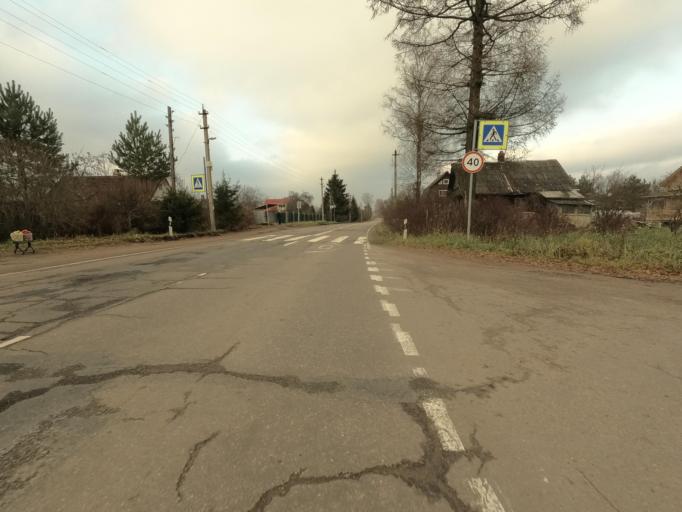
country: RU
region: Leningrad
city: Mga
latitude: 59.7742
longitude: 31.0241
